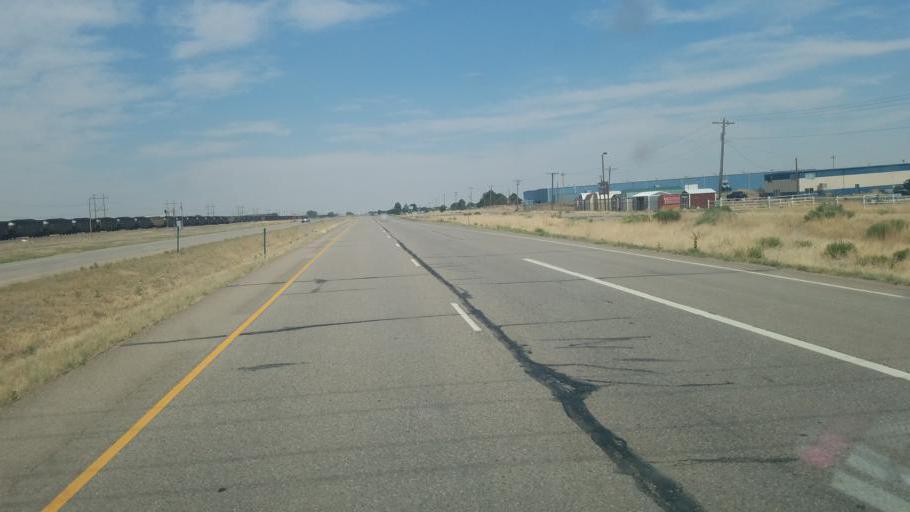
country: US
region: Colorado
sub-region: Pueblo County
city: Pueblo
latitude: 38.2742
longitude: -104.5334
